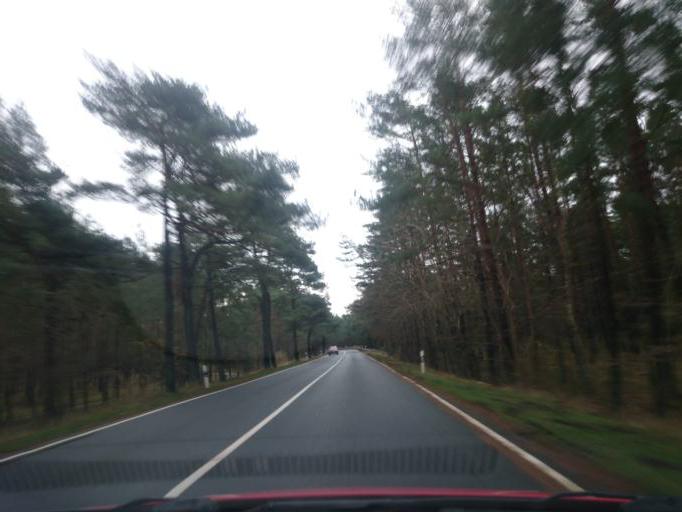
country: DE
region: Mecklenburg-Vorpommern
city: Glowe
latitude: 54.5750
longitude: 13.4189
